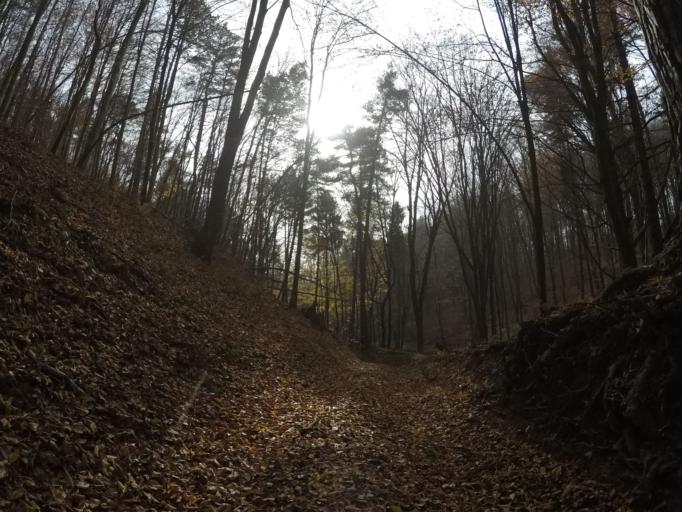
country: SK
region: Presovsky
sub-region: Okres Presov
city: Presov
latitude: 48.9458
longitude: 21.1827
